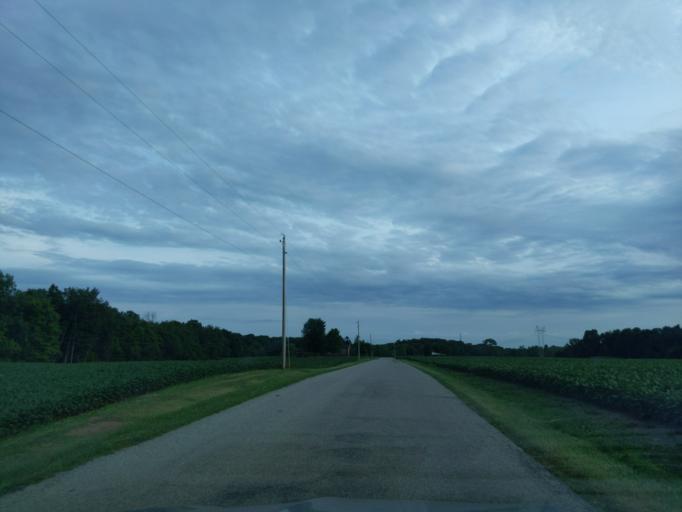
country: US
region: Indiana
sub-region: Ripley County
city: Sunman
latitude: 39.2950
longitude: -85.0903
